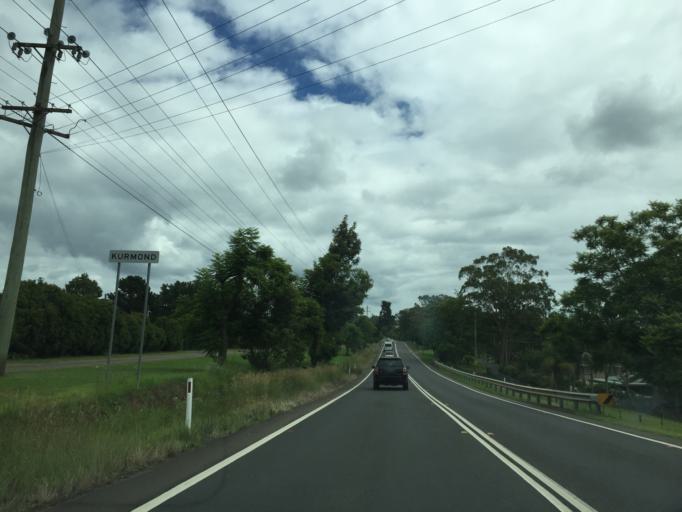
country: AU
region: New South Wales
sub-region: Hawkesbury
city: Richmond
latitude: -33.5630
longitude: 150.7030
